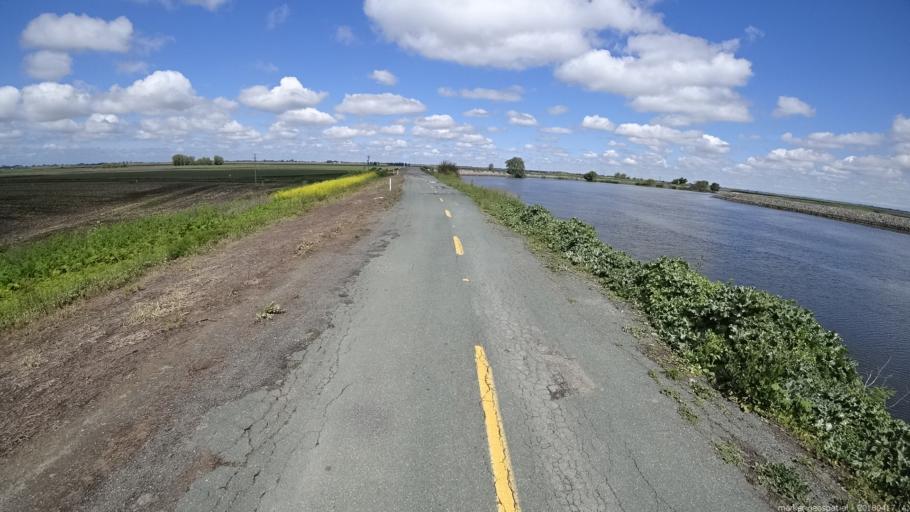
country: US
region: California
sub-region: Sacramento County
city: Walnut Grove
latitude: 38.1607
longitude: -121.5347
